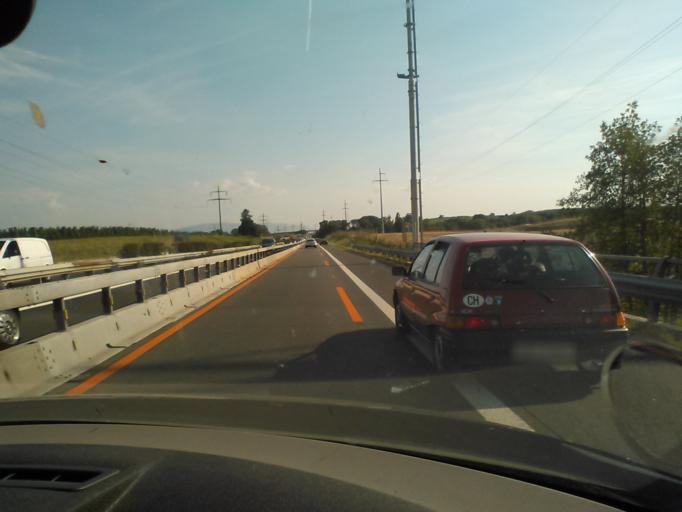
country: CH
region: Vaud
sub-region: Nyon District
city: Trelex
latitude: 46.3825
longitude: 6.2025
